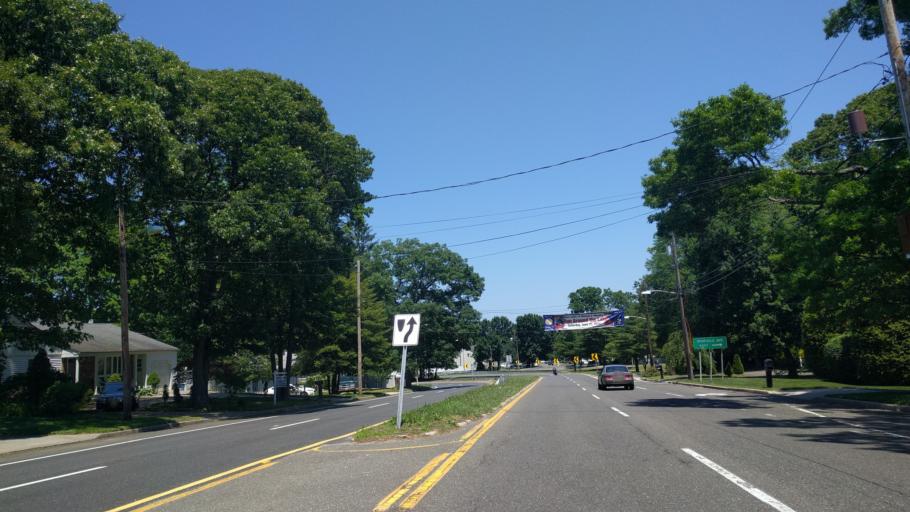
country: US
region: New York
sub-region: Suffolk County
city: Ronkonkoma
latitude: 40.8195
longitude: -73.1252
